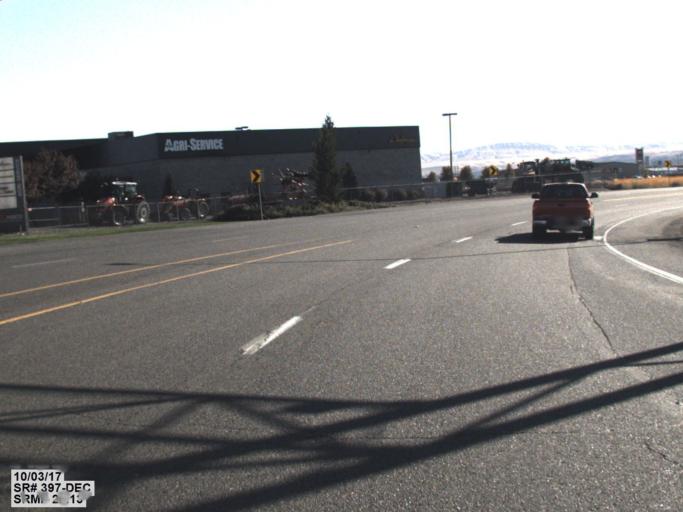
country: US
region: Washington
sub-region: Franklin County
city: Pasco
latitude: 46.2489
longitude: -119.0822
